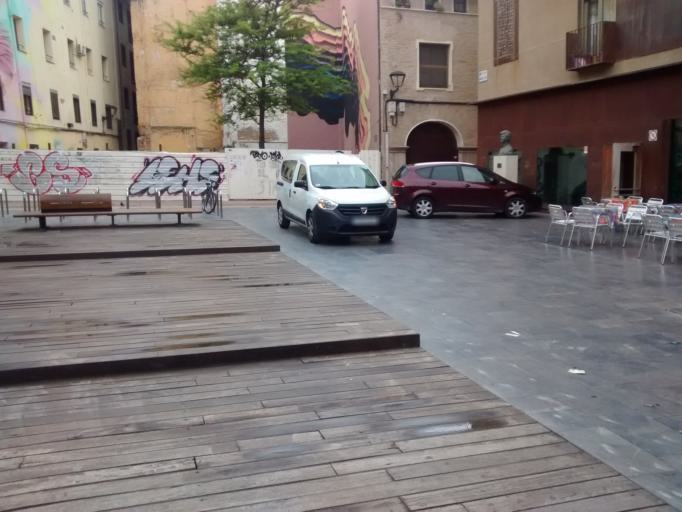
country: ES
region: Aragon
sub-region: Provincia de Zaragoza
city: Zaragoza
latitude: 41.6569
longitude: -0.8853
